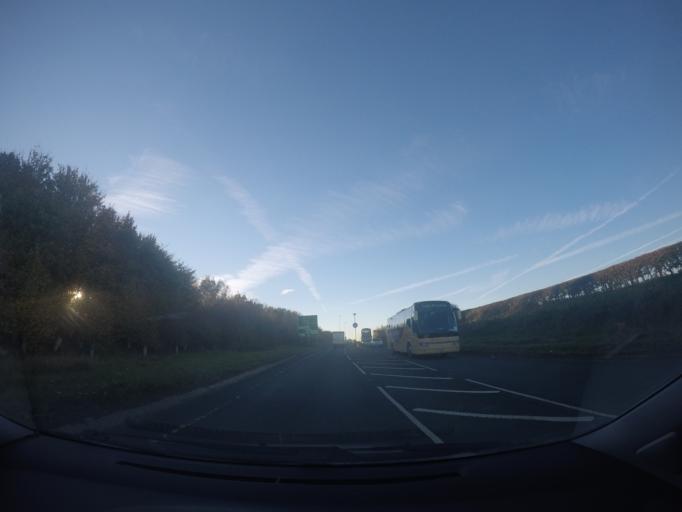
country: GB
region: England
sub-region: City of York
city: Copmanthorpe
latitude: 53.9390
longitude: -1.1450
